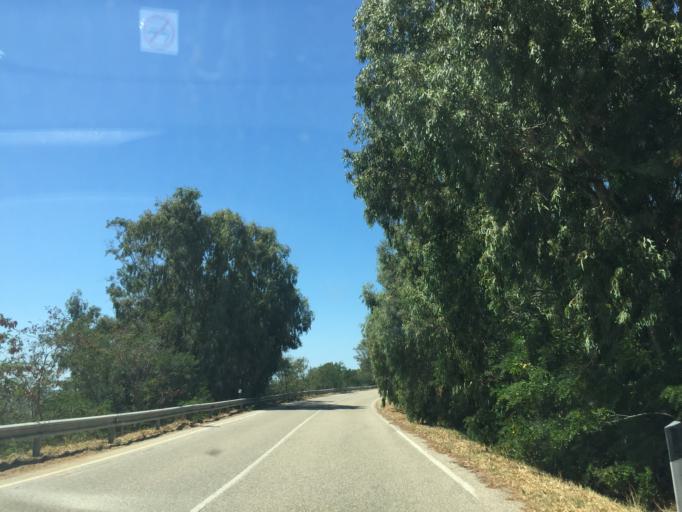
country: IT
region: Sardinia
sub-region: Provincia di Olbia-Tempio
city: Aglientu
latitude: 41.0984
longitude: 9.0864
